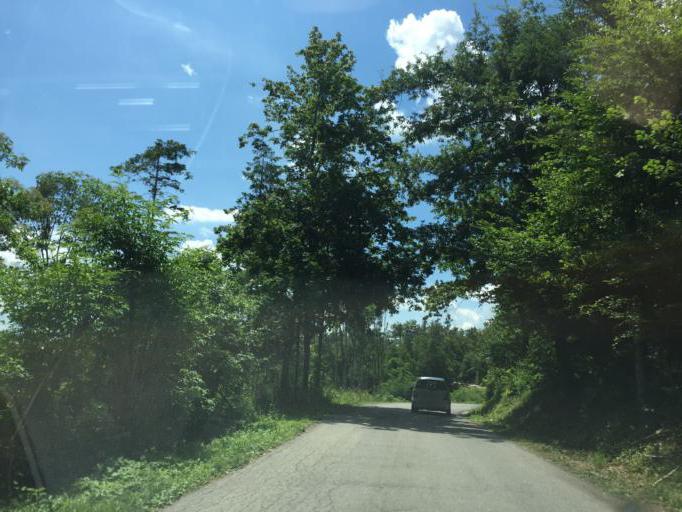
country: SI
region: Postojna
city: Postojna
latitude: 45.8083
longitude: 14.1503
